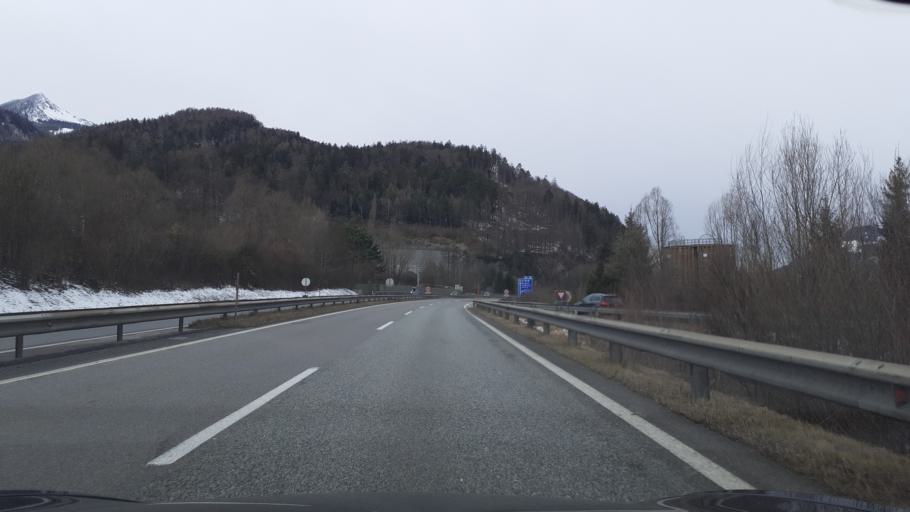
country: AT
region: Vorarlberg
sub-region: Politischer Bezirk Bludenz
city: Nuziders
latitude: 47.1592
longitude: 9.8021
